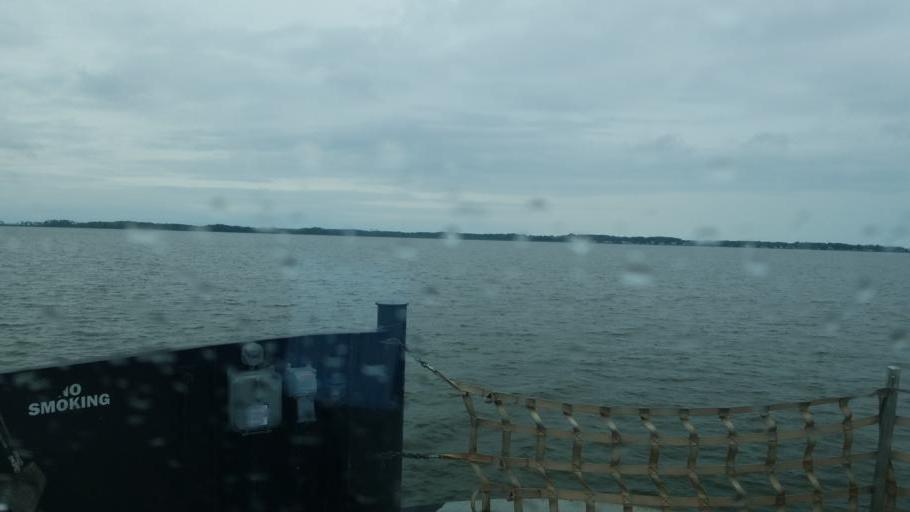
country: US
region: North Carolina
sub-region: Currituck County
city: Currituck
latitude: 36.4722
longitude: -75.9504
